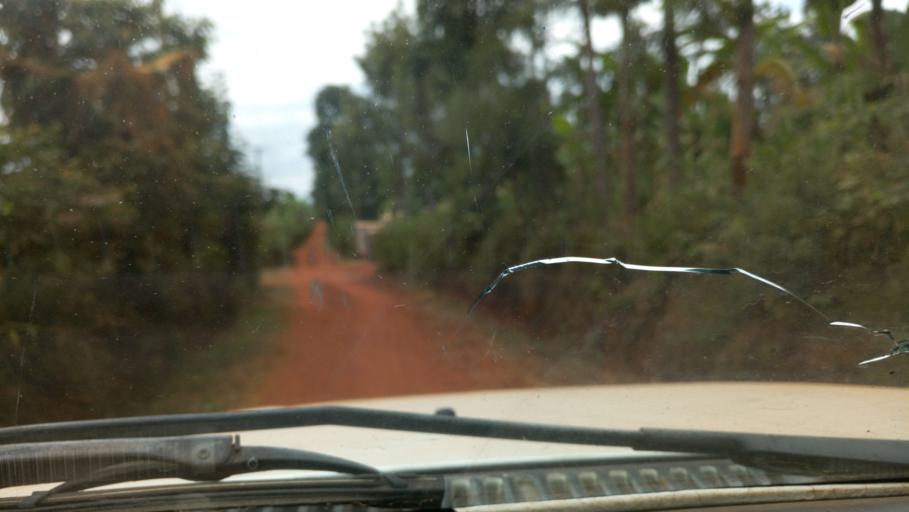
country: KE
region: Murang'a District
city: Maragua
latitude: -0.7637
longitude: 37.1149
